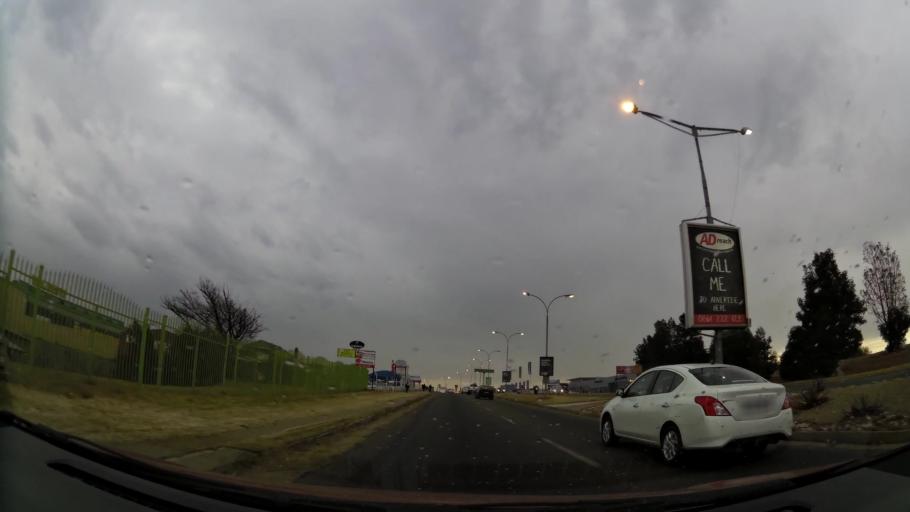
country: ZA
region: Gauteng
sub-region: City of Johannesburg Metropolitan Municipality
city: Roodepoort
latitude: -26.1284
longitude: 27.8490
